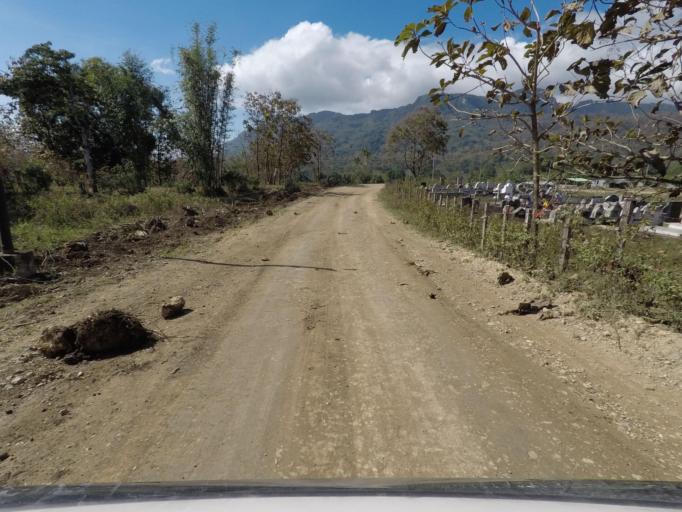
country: TL
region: Baucau
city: Venilale
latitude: -8.6609
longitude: 126.3716
